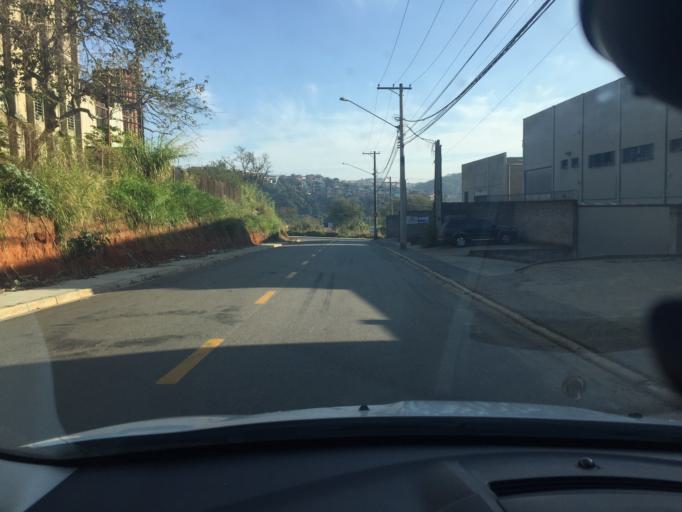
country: BR
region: Sao Paulo
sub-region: Varzea Paulista
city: Varzea Paulista
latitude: -23.2050
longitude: -46.8138
